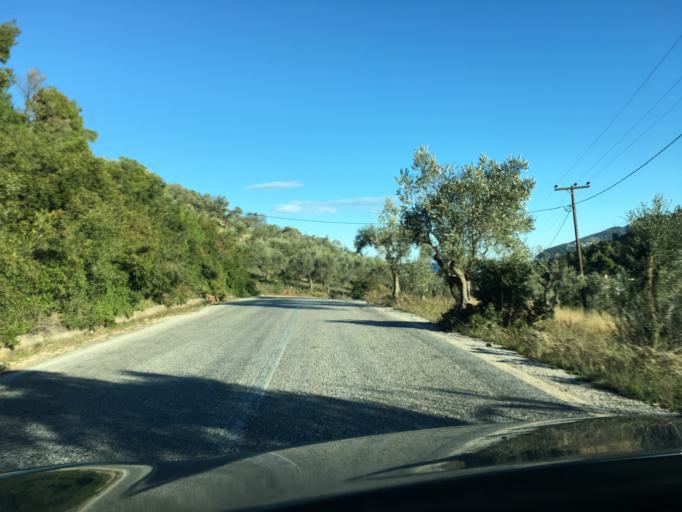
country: GR
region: Thessaly
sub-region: Nomos Magnisias
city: Skopelos
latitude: 39.1002
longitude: 23.7206
